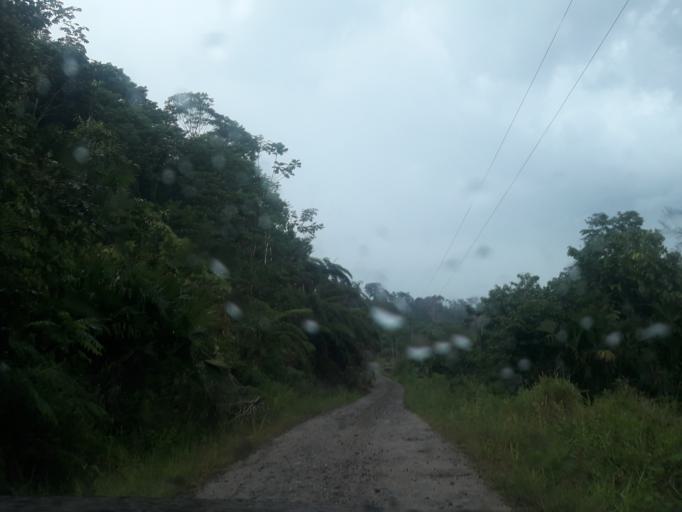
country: EC
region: Napo
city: Tena
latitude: -1.0996
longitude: -77.6899
